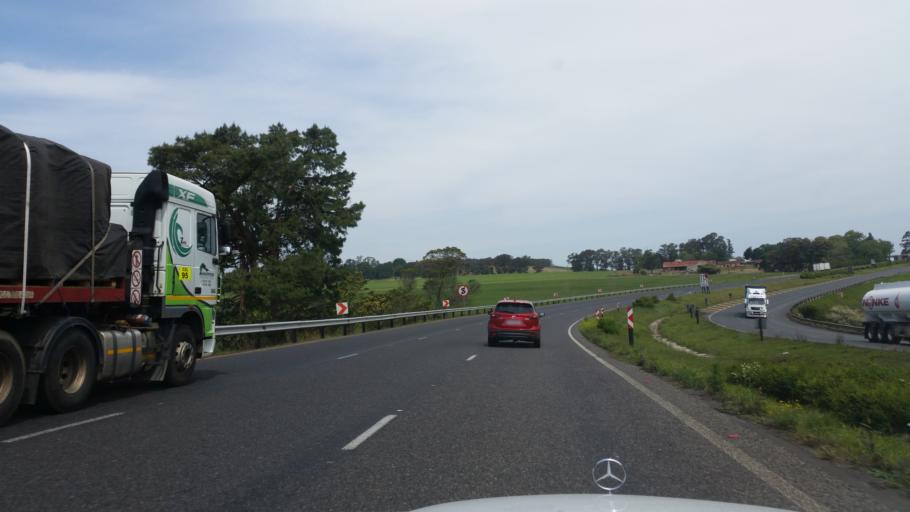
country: ZA
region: KwaZulu-Natal
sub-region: uMgungundlovu District Municipality
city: Howick
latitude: -29.4451
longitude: 30.1772
